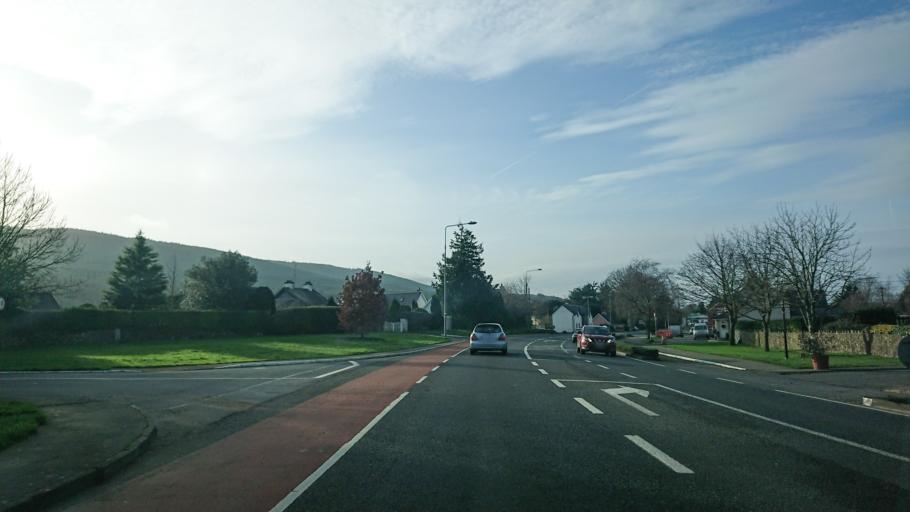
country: IE
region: Munster
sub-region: South Tipperary
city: Cluain Meala
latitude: 52.3610
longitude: -7.5749
